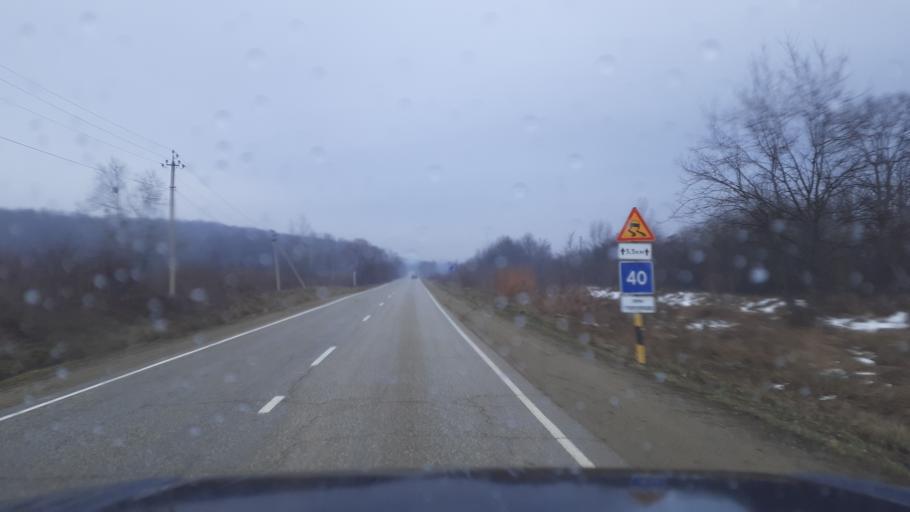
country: RU
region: Krasnodarskiy
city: Neftegorsk
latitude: 44.2611
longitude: 39.7753
